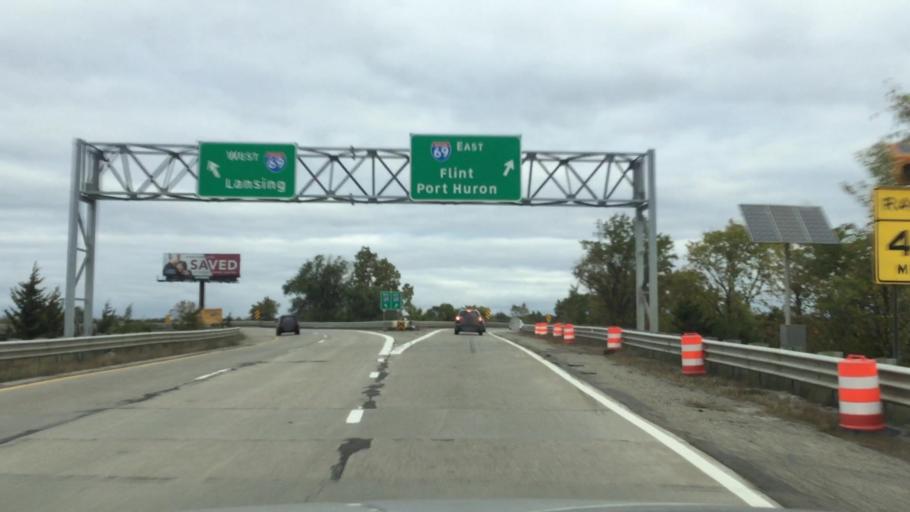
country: US
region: Michigan
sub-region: Genesee County
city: Flint
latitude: 42.9815
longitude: -83.7288
